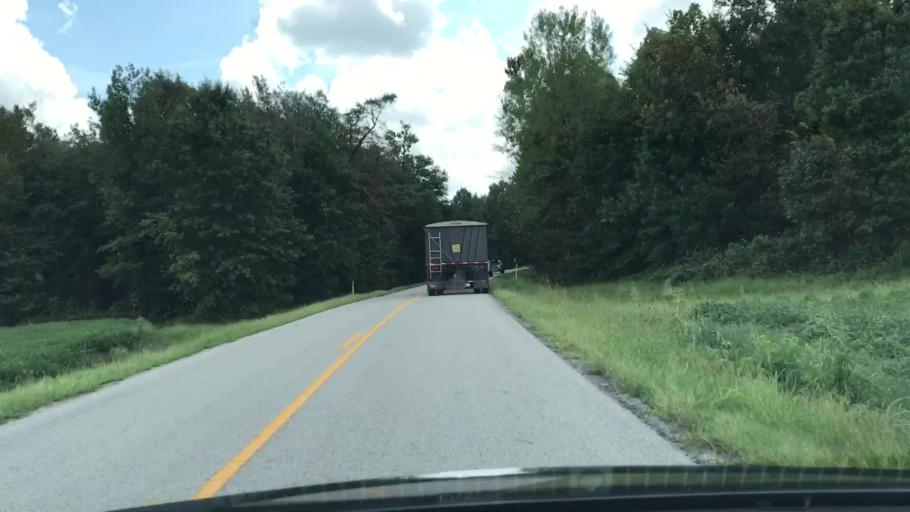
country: US
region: Kentucky
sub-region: Todd County
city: Guthrie
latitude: 36.6829
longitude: -87.0241
